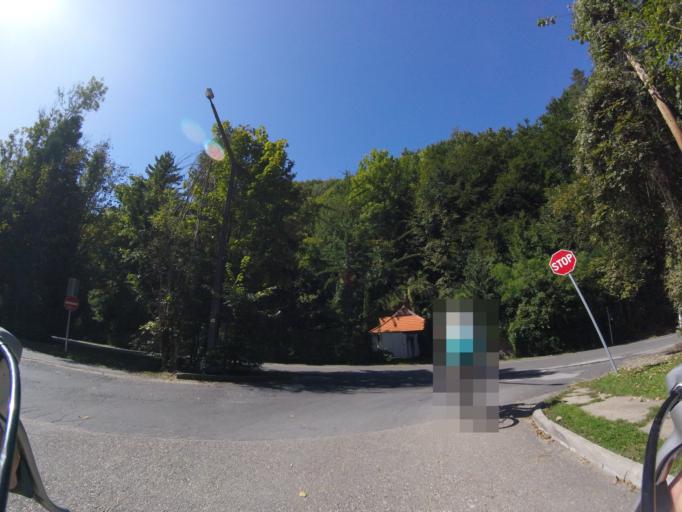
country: HU
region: Borsod-Abauj-Zemplen
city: Sajobabony
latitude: 48.0943
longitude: 20.6199
